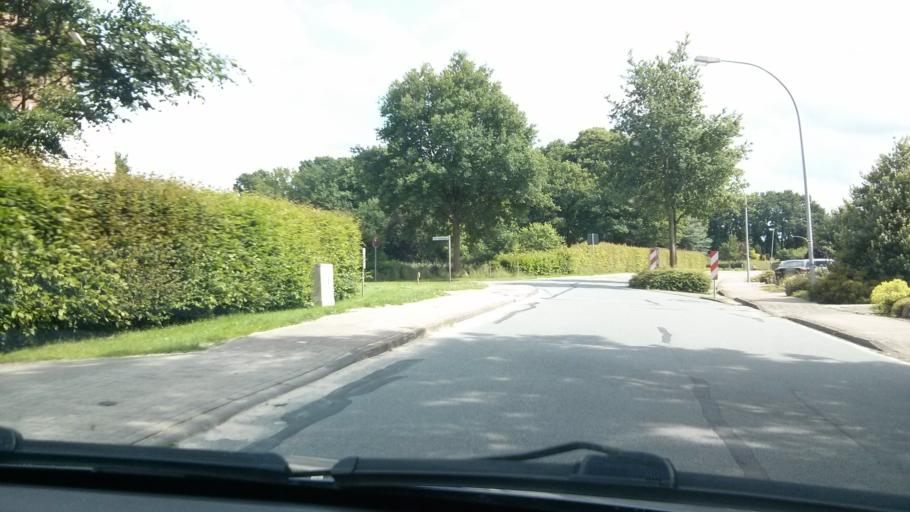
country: DE
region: Lower Saxony
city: Schiffdorf
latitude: 53.5292
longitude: 8.6564
